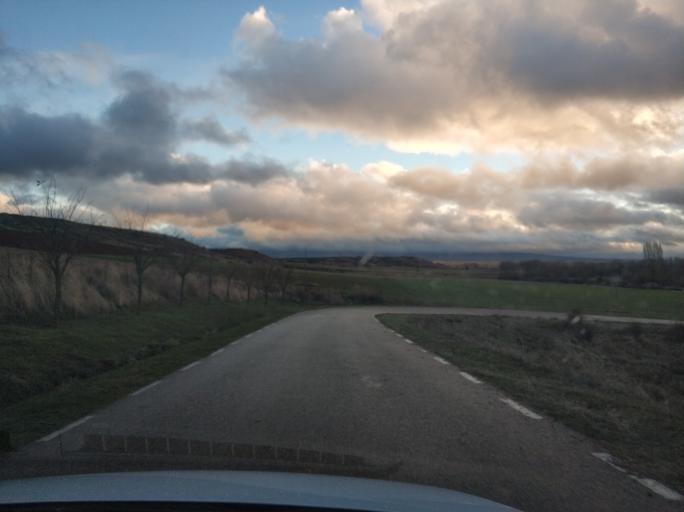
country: ES
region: Castille and Leon
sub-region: Provincia de Segovia
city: Ayllon
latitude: 41.4132
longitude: -3.4068
